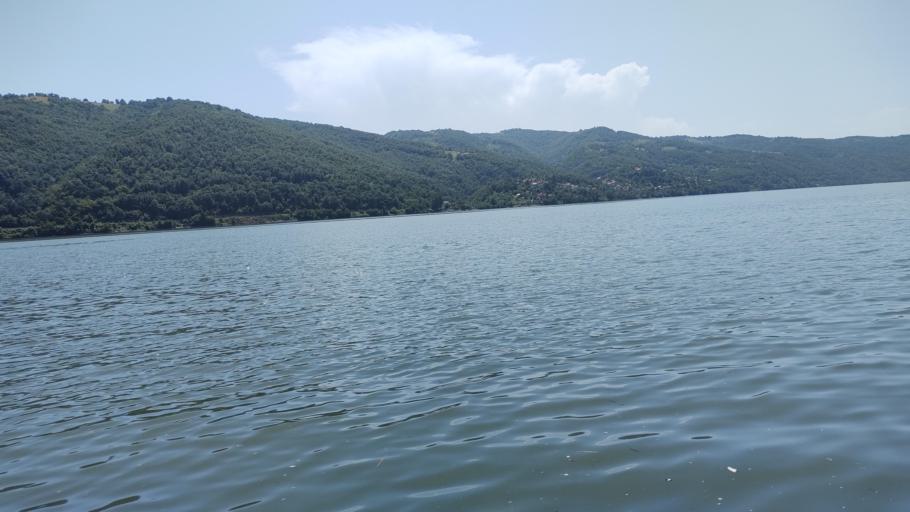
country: RO
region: Mehedinti
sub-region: Comuna Svinita
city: Svinita
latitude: 44.5135
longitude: 22.1974
